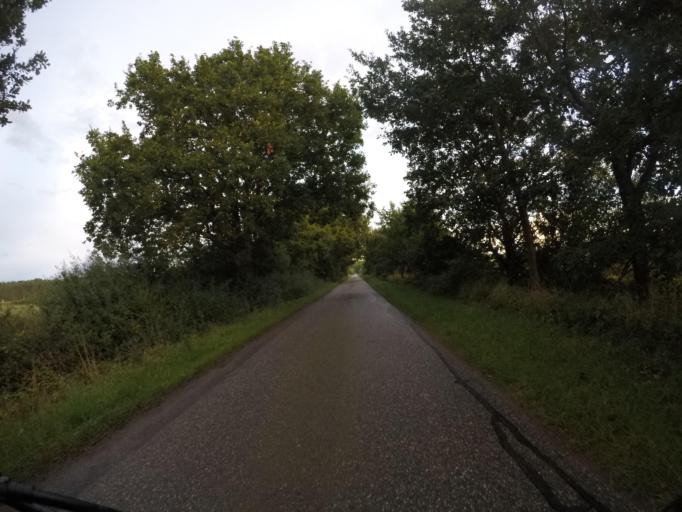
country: DE
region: Lower Saxony
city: Neu Darchau
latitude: 53.2635
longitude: 10.9064
